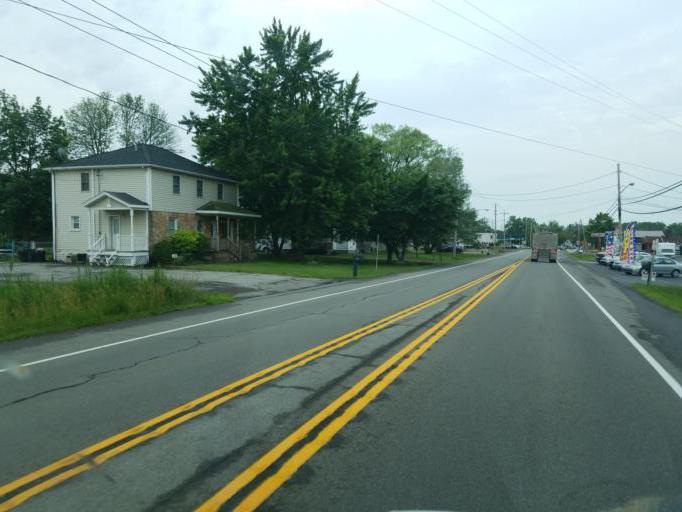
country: US
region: New York
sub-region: Niagara County
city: Lewiston
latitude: 43.1318
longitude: -79.0040
